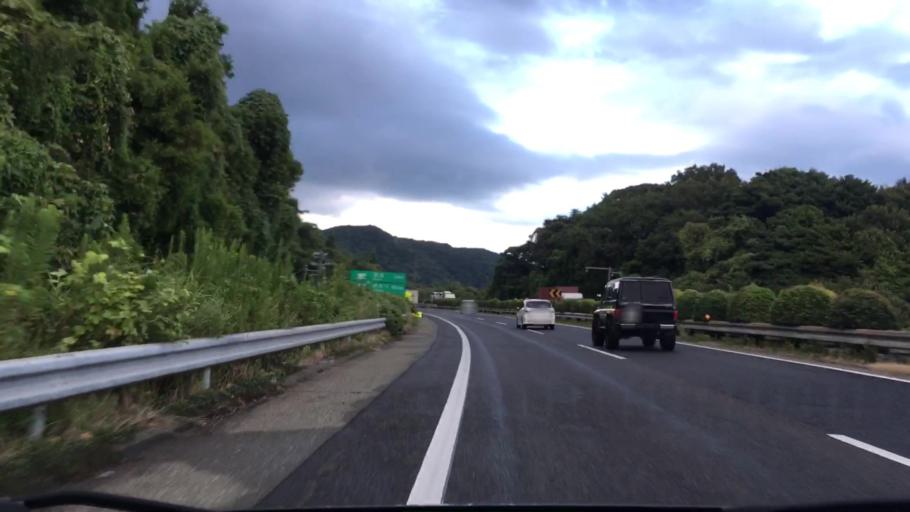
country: JP
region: Fukuoka
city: Kanda
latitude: 33.8546
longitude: 130.9370
